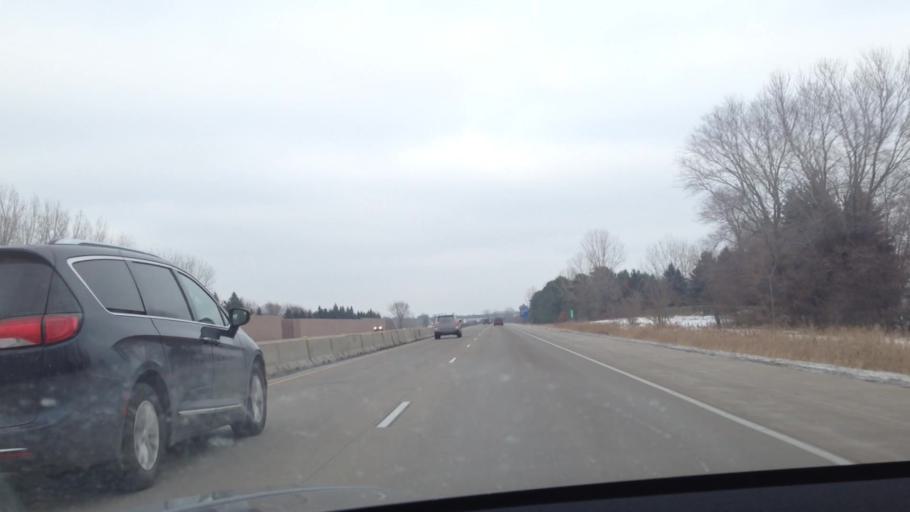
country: US
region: Minnesota
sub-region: Anoka County
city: Circle Pines
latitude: 45.1688
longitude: -93.1397
